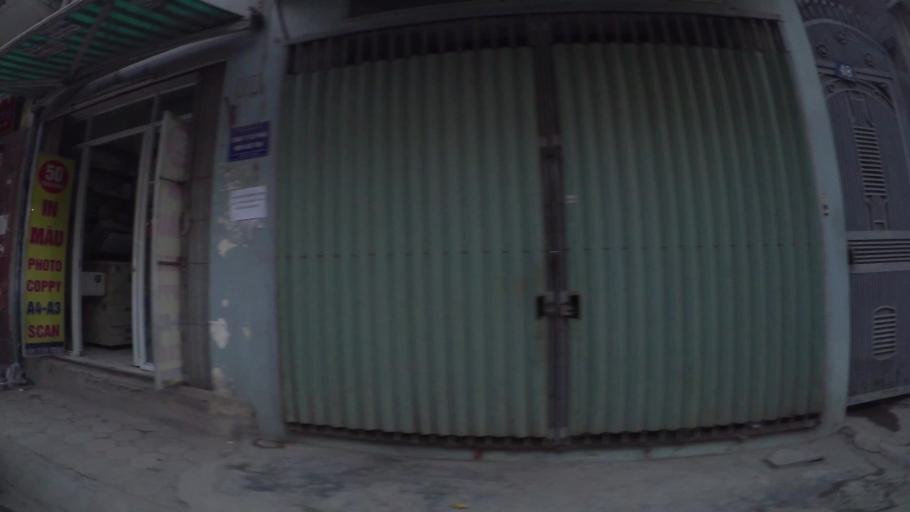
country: VN
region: Ha Noi
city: Thanh Xuan
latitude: 20.9855
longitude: 105.7988
